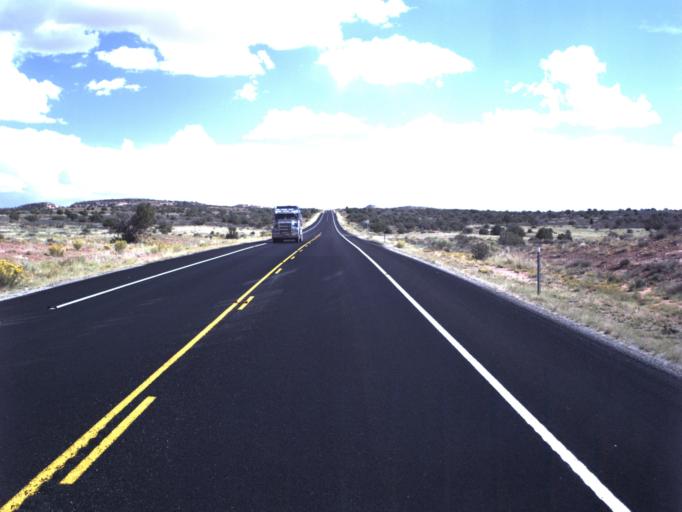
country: US
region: Utah
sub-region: Grand County
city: Moab
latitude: 38.6027
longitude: -109.8165
